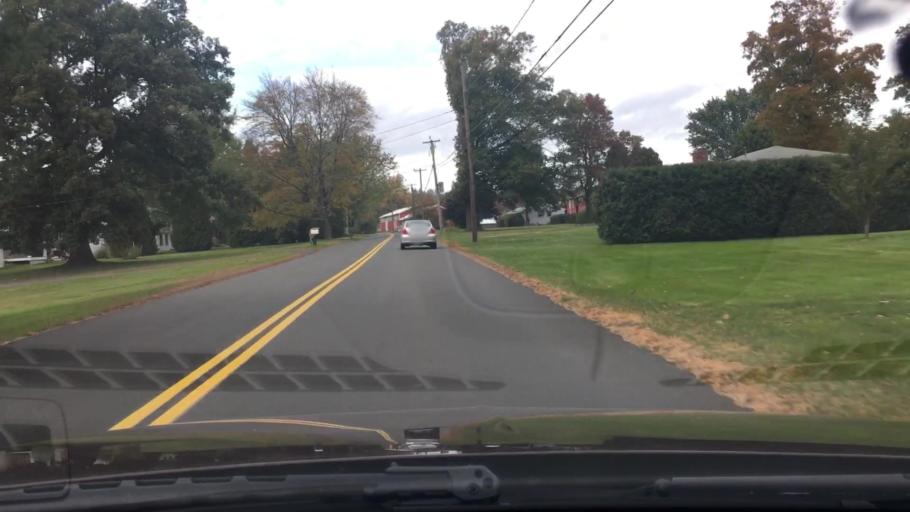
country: US
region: Connecticut
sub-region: Tolland County
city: Ellington
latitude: 41.9359
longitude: -72.4782
